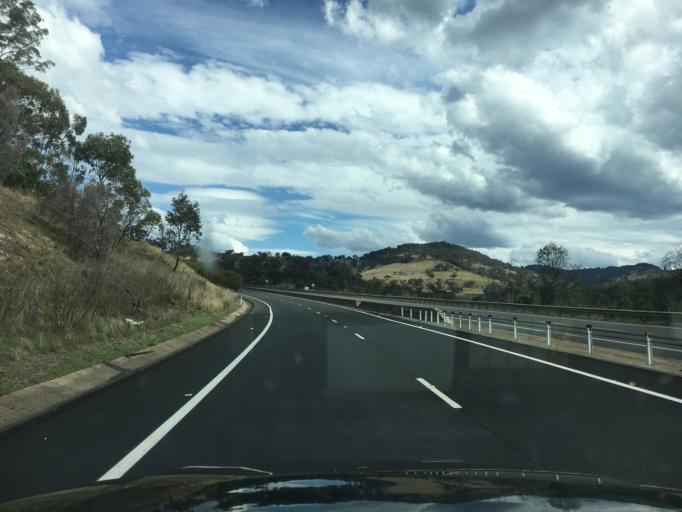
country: AU
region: New South Wales
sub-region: Liverpool Plains
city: Quirindi
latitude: -31.7309
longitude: 150.7840
